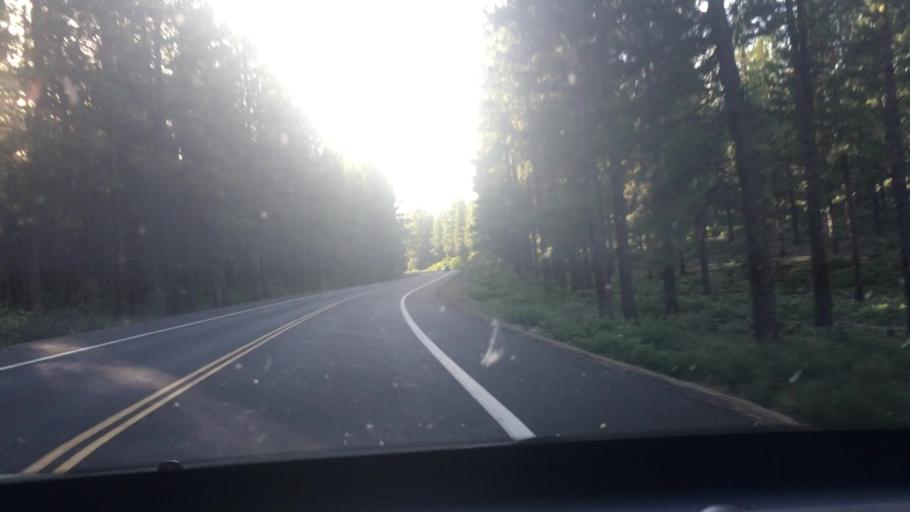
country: US
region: Oregon
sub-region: Deschutes County
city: Deschutes River Woods
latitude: 44.0374
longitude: -121.4615
